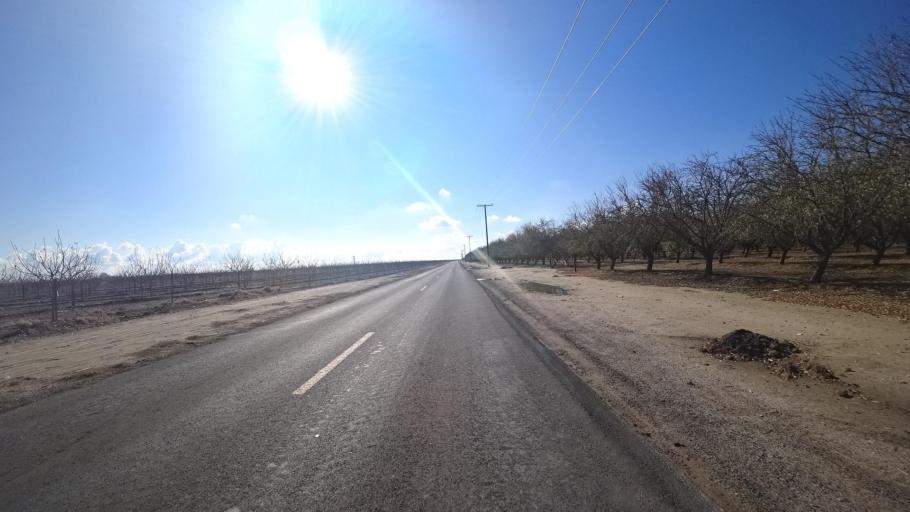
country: US
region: California
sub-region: Kern County
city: Delano
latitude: 35.7363
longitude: -119.2584
